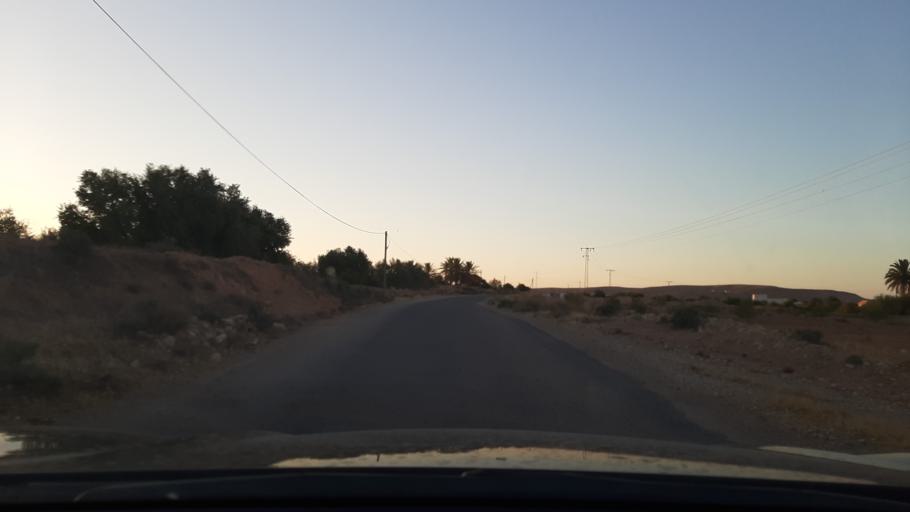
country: TN
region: Qabis
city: Matmata
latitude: 33.5574
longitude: 10.1843
